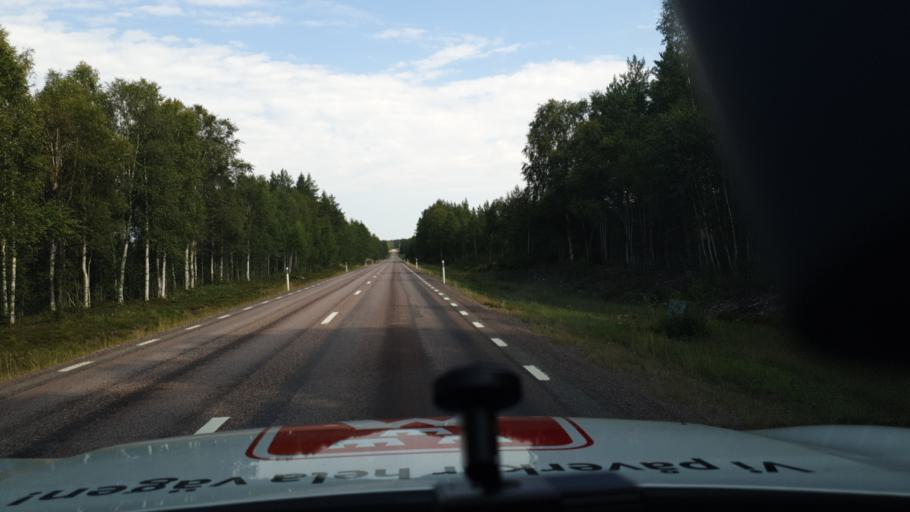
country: SE
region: Vaermland
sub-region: Hagfors Kommun
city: Ekshaerad
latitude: 60.4640
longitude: 13.2992
